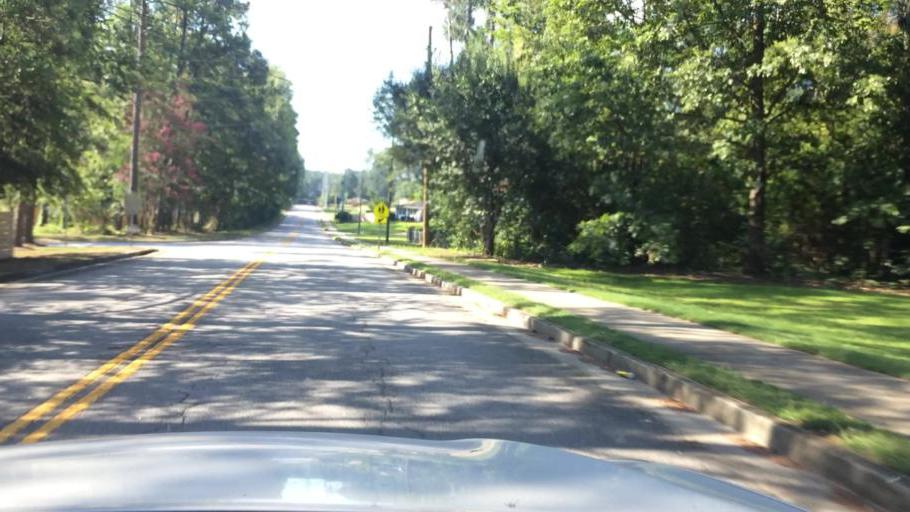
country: US
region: Georgia
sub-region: Columbia County
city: Martinez
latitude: 33.4990
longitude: -82.0398
